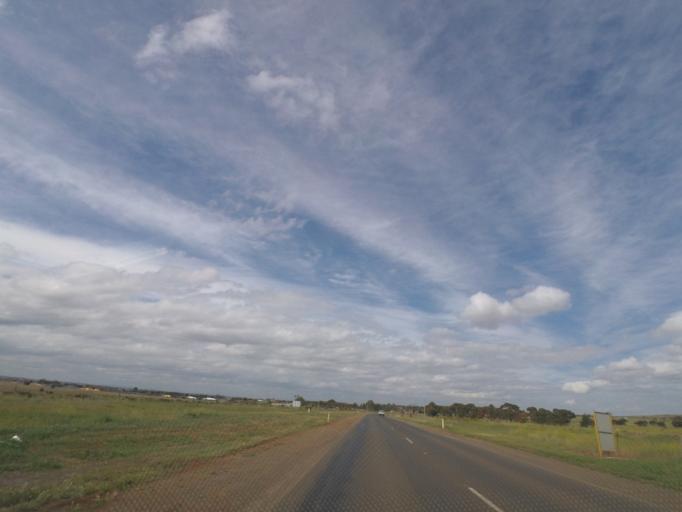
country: AU
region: Victoria
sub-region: Melton
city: Rockbank
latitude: -37.7443
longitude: 144.6606
